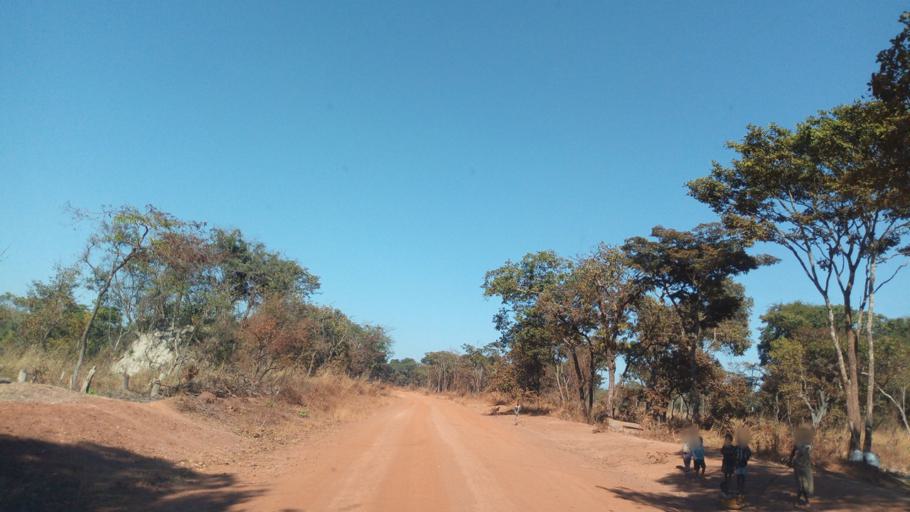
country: ZM
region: Luapula
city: Mwense
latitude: -10.7080
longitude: 28.3681
